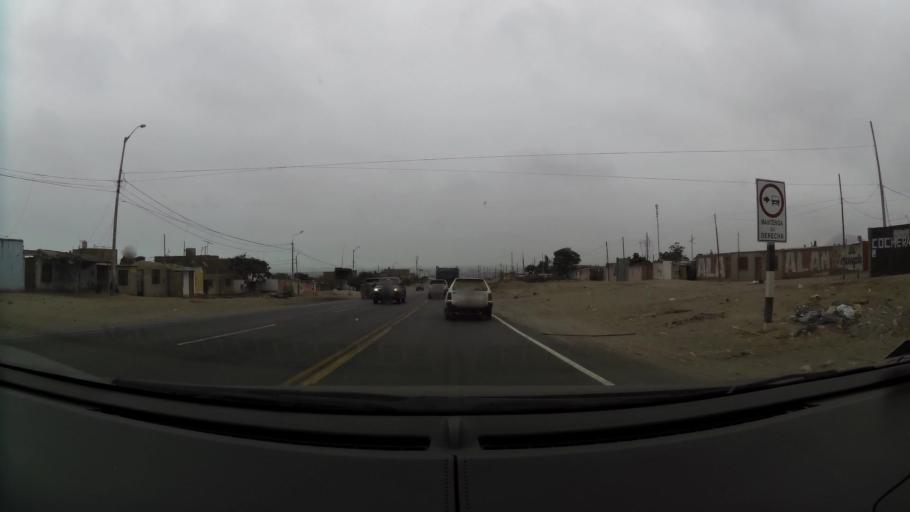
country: PE
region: La Libertad
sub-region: Provincia de Trujillo
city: Moche
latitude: -8.1851
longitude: -78.9837
